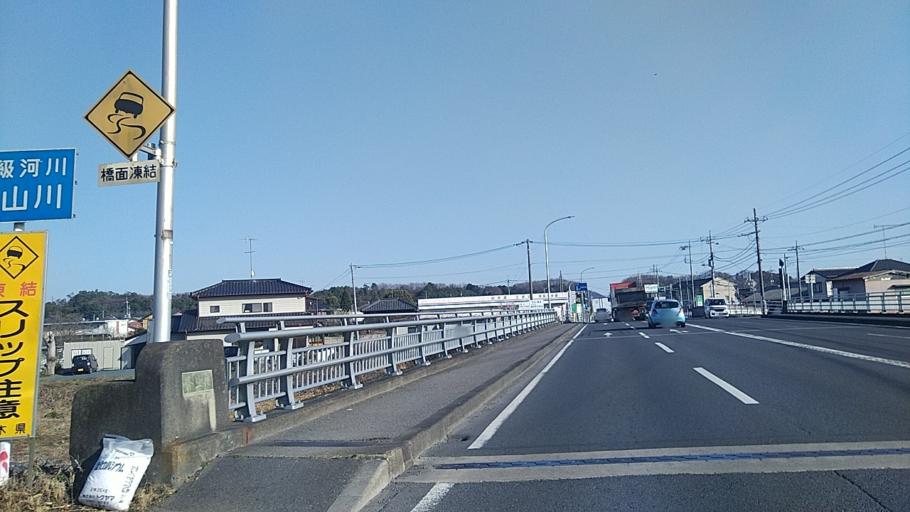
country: JP
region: Tochigi
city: Sano
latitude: 36.3361
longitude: 139.5795
